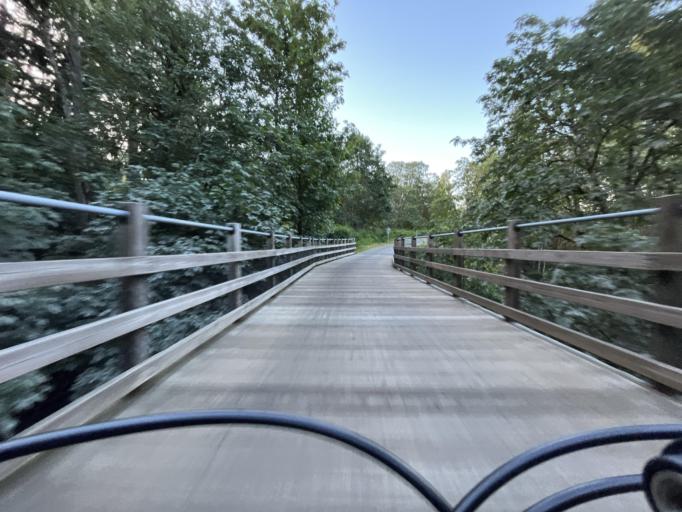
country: CA
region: British Columbia
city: Colwood
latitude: 48.4474
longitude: -123.4734
